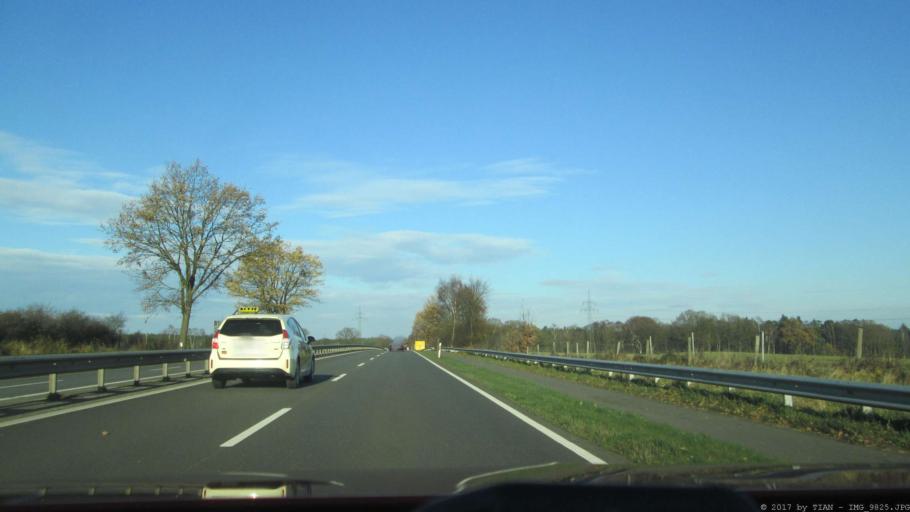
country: DE
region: Lower Saxony
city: Melbeck
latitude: 53.1936
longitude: 10.4053
